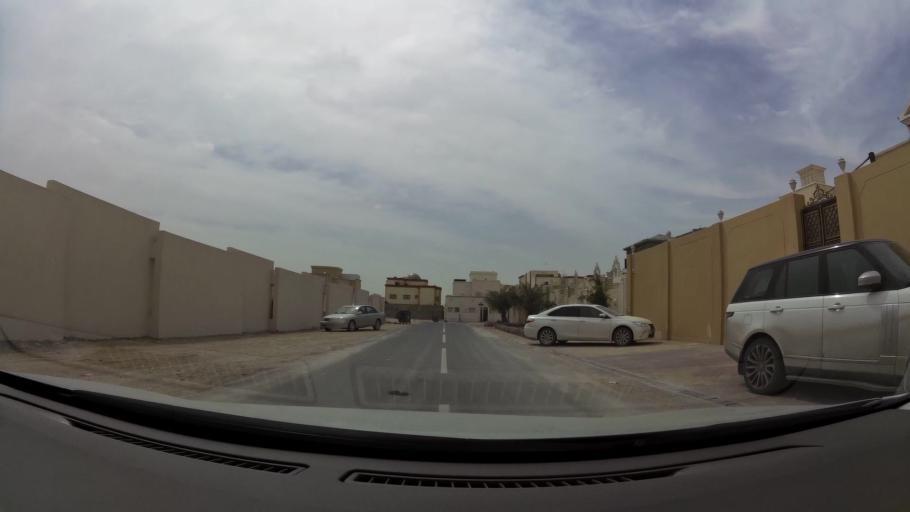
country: QA
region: Baladiyat ad Dawhah
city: Doha
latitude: 25.2180
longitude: 51.4666
